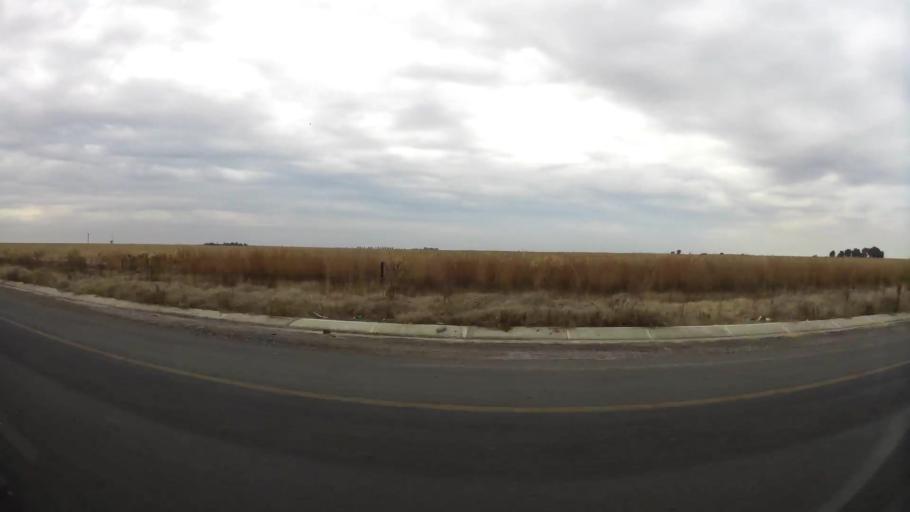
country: ZA
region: Orange Free State
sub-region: Fezile Dabi District Municipality
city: Kroonstad
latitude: -27.6183
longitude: 27.2353
